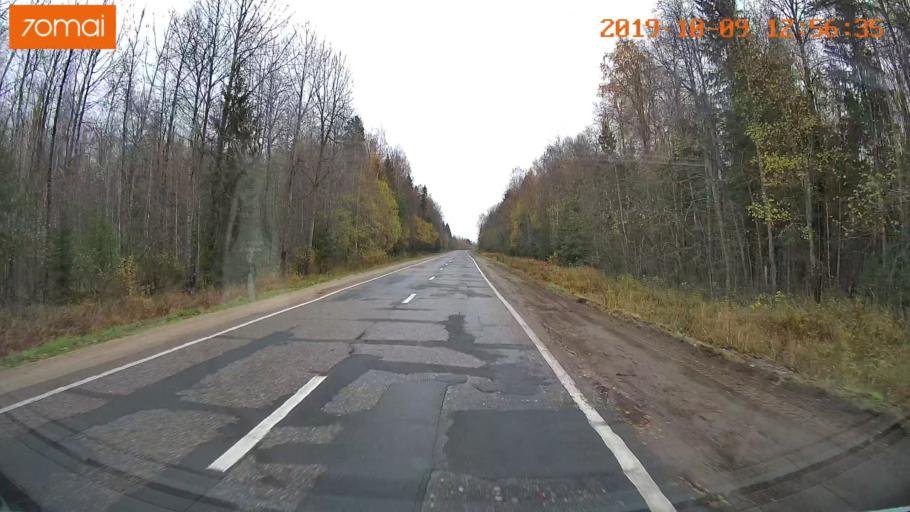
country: RU
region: Jaroslavl
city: Prechistoye
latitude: 58.3945
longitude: 40.4186
